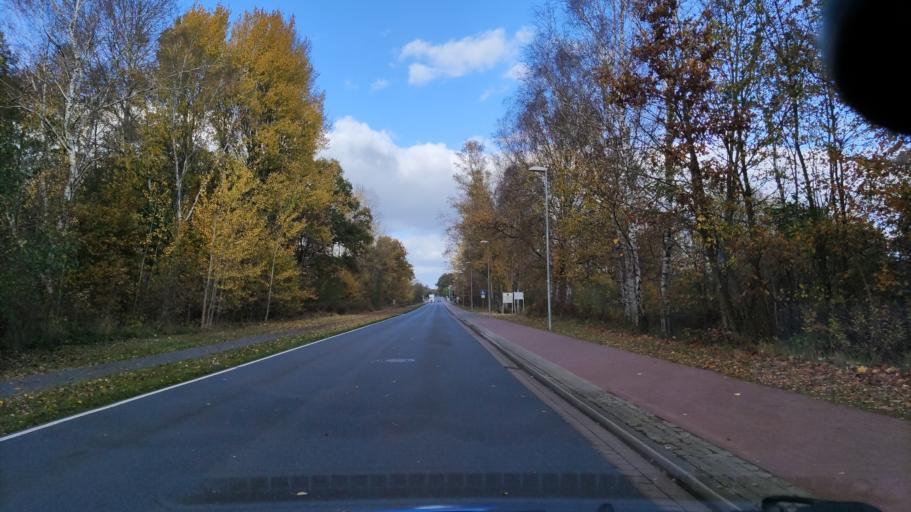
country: DE
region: Lower Saxony
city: Munster
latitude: 52.9984
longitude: 10.0897
